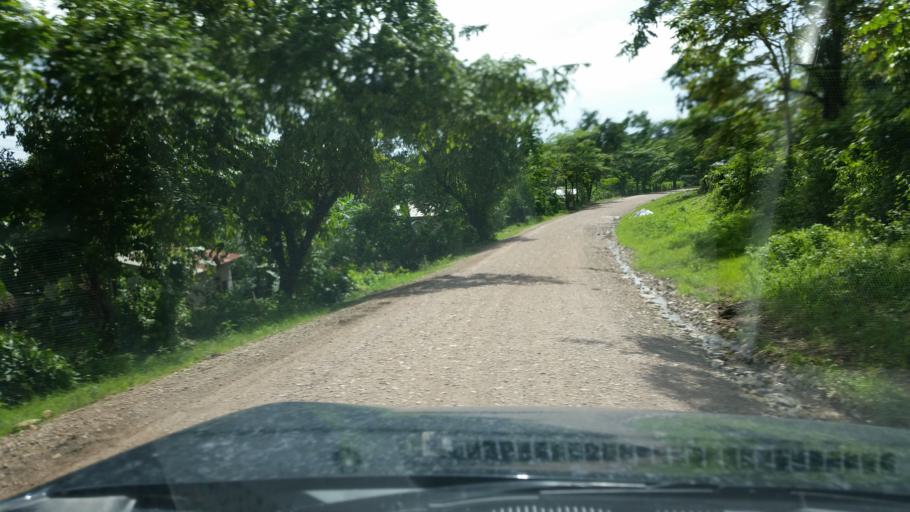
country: NI
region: Atlantico Norte (RAAN)
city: Siuna
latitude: 13.6812
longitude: -84.6553
